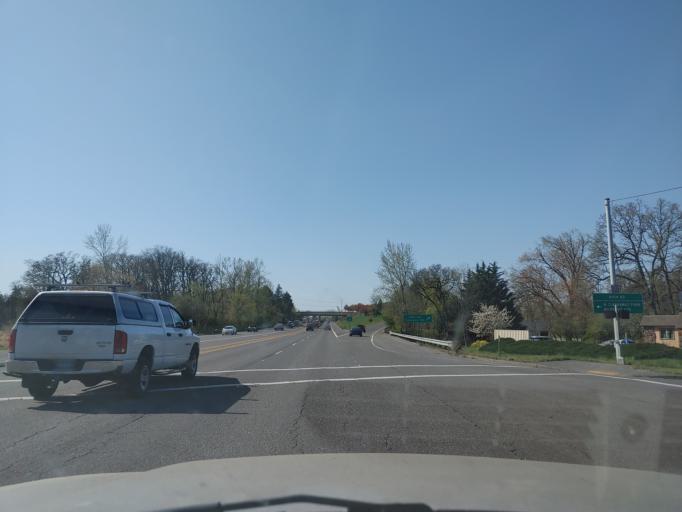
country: US
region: Oregon
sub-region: Clackamas County
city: Oatfield
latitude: 45.4279
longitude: -122.6014
